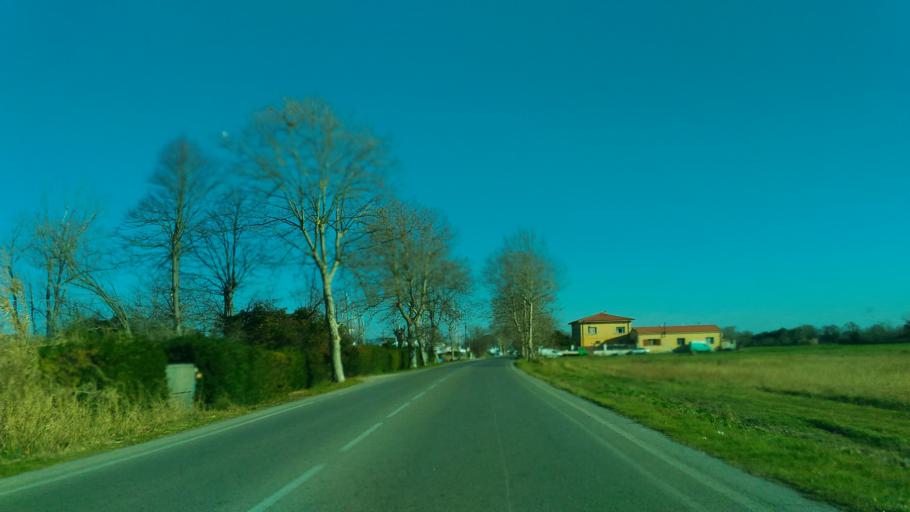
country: IT
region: Tuscany
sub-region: Province of Pisa
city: Marina di Pisa
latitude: 43.6792
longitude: 10.2816
